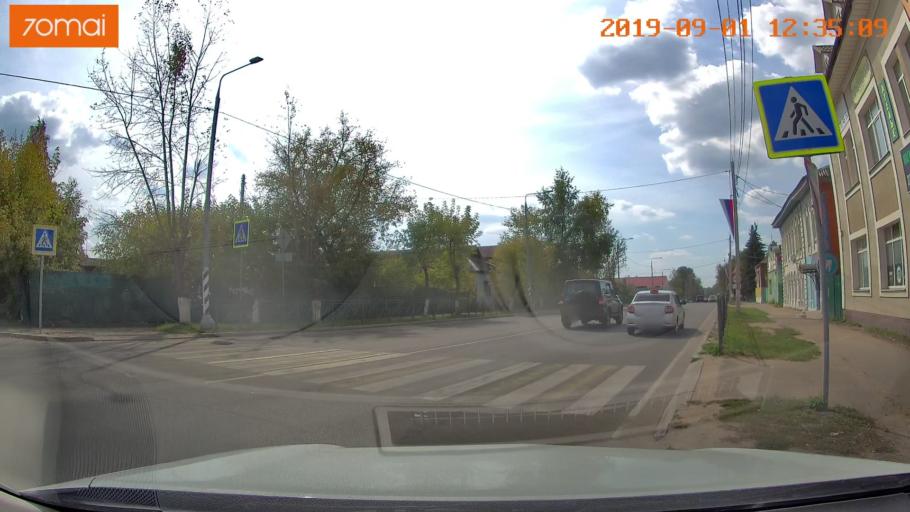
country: RU
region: Kaluga
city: Maloyaroslavets
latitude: 55.0110
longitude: 36.4561
